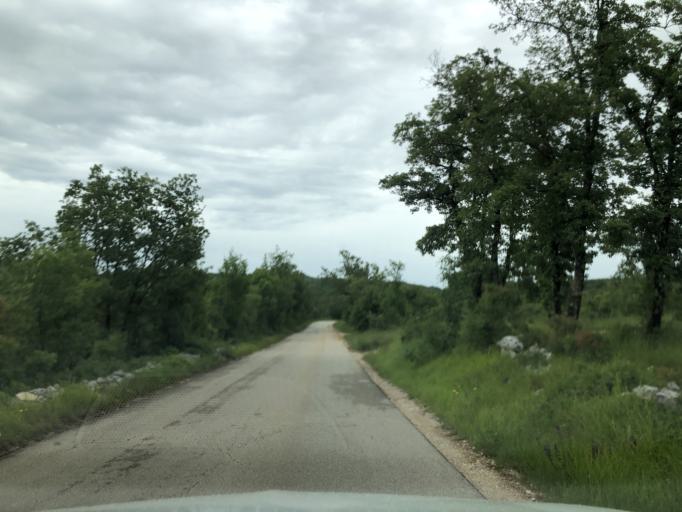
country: HR
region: Istarska
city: Buje
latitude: 45.4363
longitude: 13.6736
